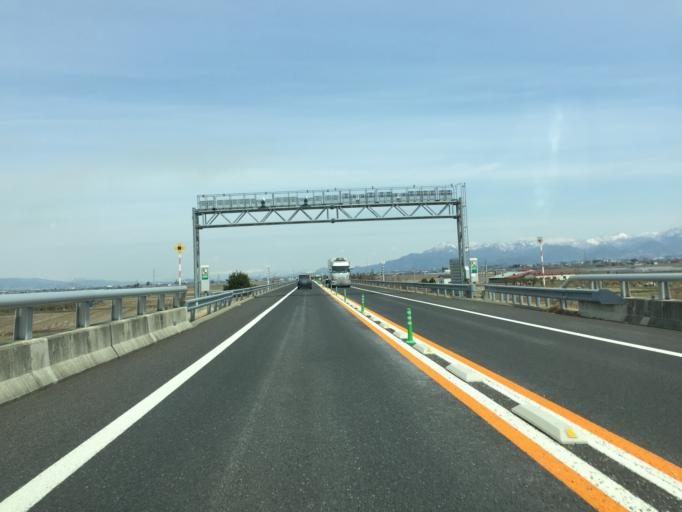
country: JP
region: Yamagata
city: Tendo
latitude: 38.3387
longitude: 140.3324
